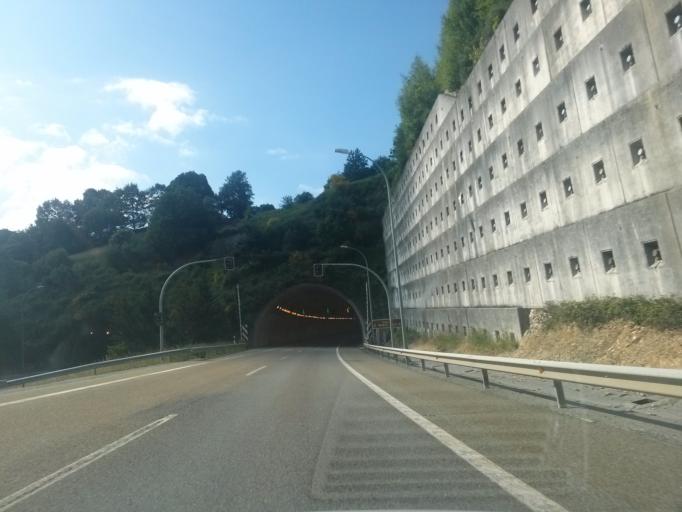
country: ES
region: Castille and Leon
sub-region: Provincia de Leon
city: Balboa
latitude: 42.7328
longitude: -7.0447
